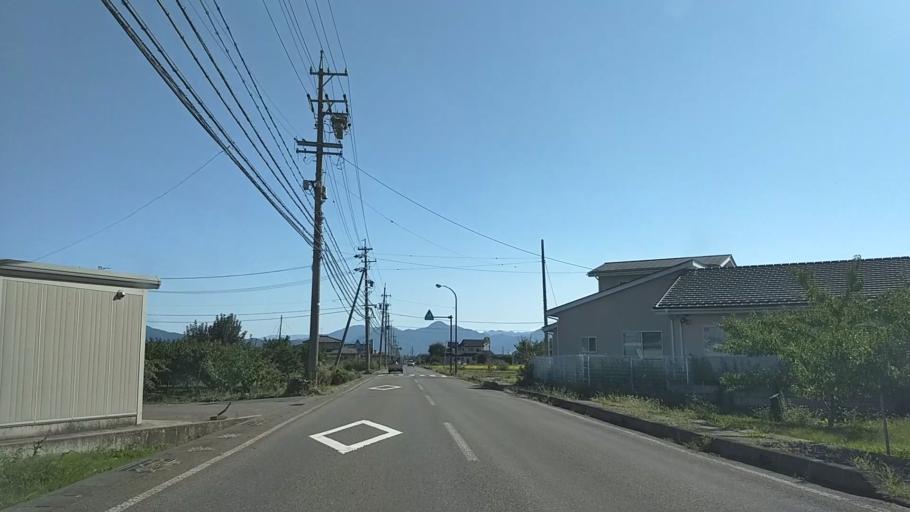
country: JP
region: Nagano
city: Nagano-shi
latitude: 36.6084
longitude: 138.1436
